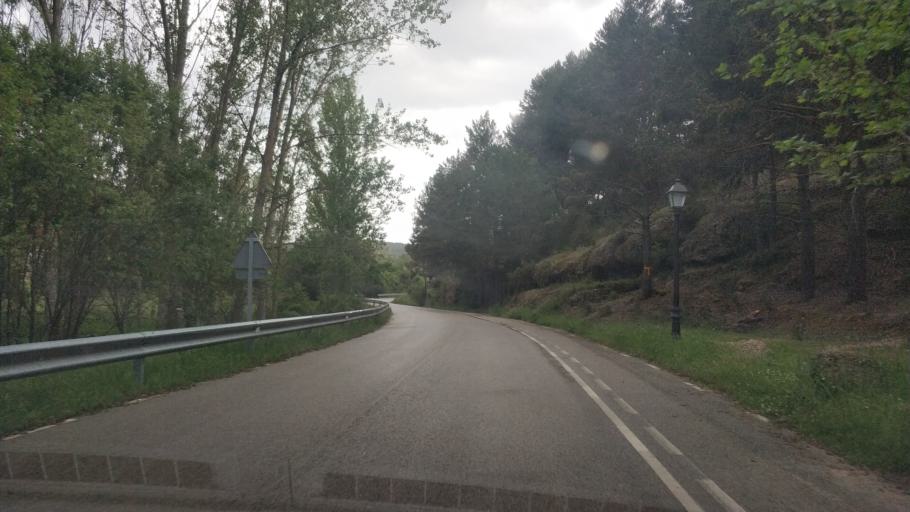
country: ES
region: Castille and Leon
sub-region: Provincia de Soria
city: San Leonardo de Yague
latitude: 41.8359
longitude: -3.0660
